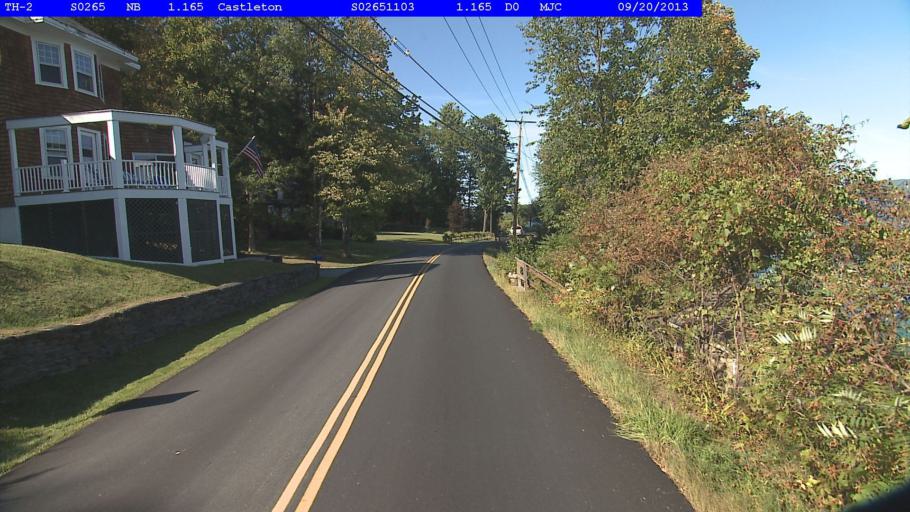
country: US
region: Vermont
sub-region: Rutland County
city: Fair Haven
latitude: 43.6207
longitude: -73.2300
